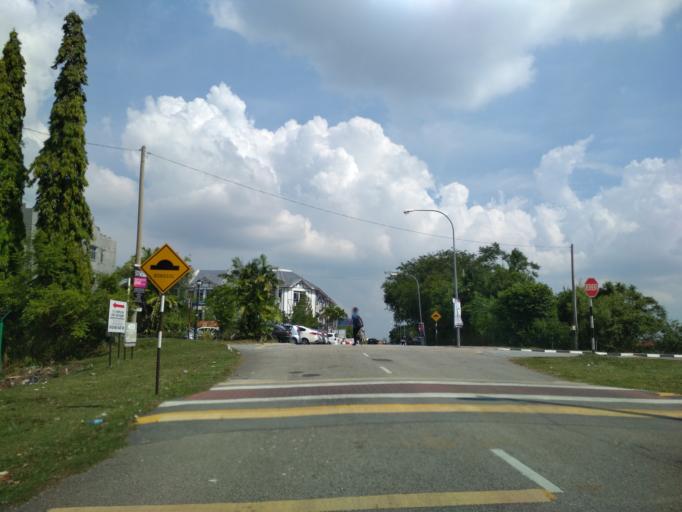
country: MY
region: Perak
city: Kampar
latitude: 4.3296
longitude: 101.1435
